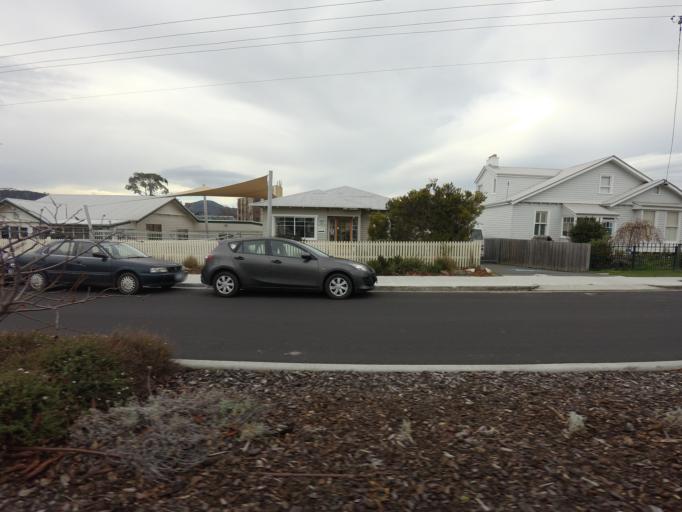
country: AU
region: Tasmania
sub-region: Clarence
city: Bellerive
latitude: -42.8758
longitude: 147.3674
